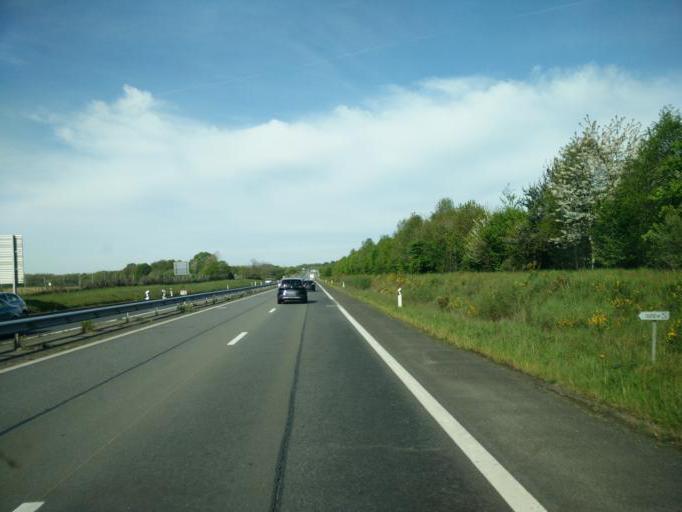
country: FR
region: Brittany
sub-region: Departement d'Ille-et-Vilaine
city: Roz-sur-Couesnon
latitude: 48.5663
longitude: -1.5922
